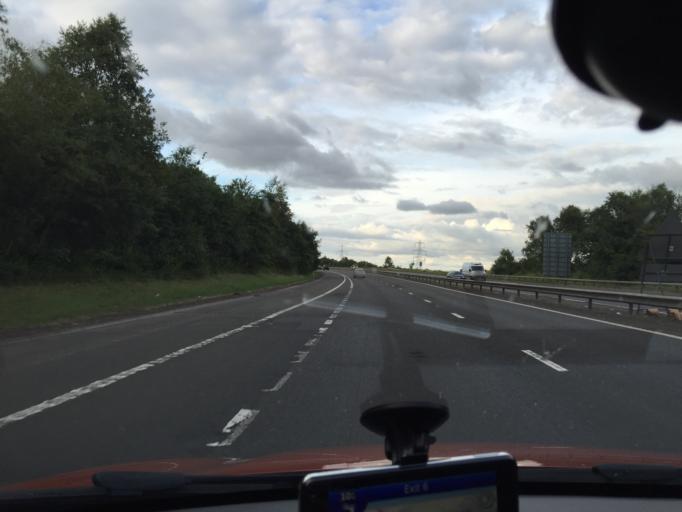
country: GB
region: Scotland
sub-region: North Lanarkshire
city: Glenboig
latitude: 55.8935
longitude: -4.0707
